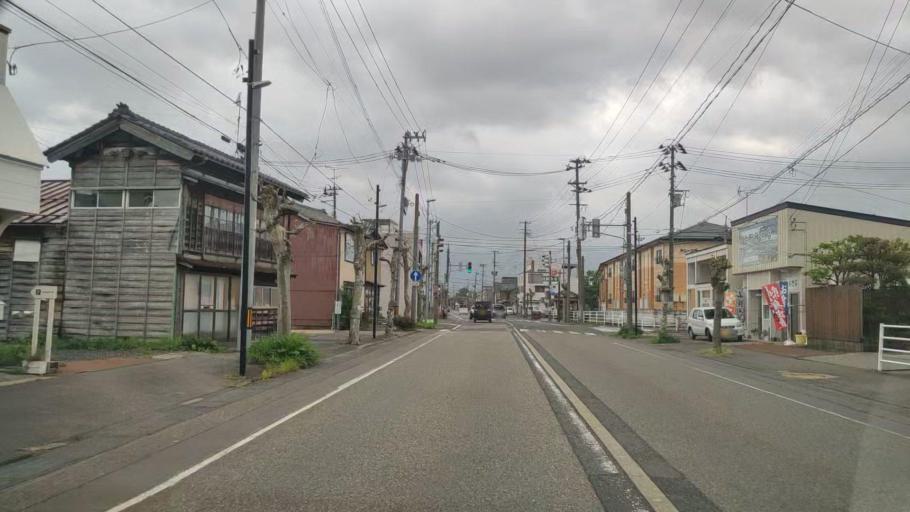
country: JP
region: Niigata
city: Gosen
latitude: 37.7376
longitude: 139.1822
